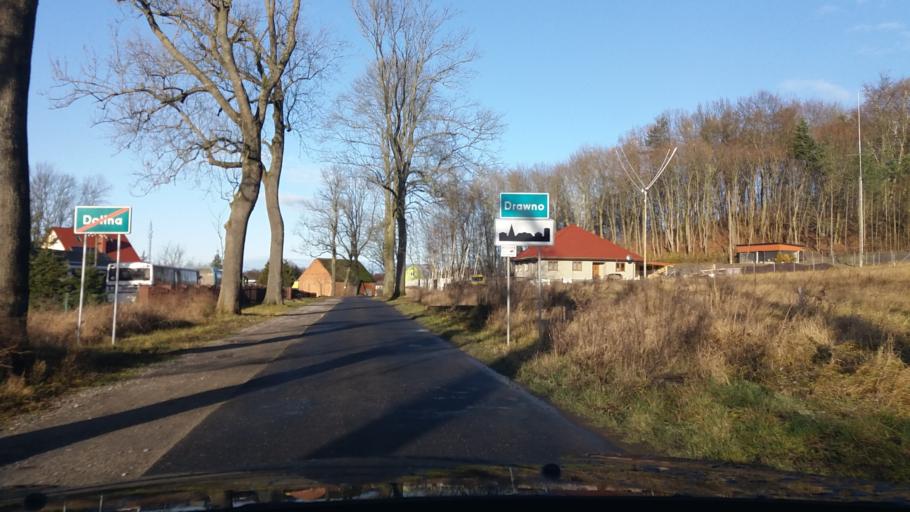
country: PL
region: West Pomeranian Voivodeship
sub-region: Powiat choszczenski
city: Drawno
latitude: 53.2107
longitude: 15.7720
